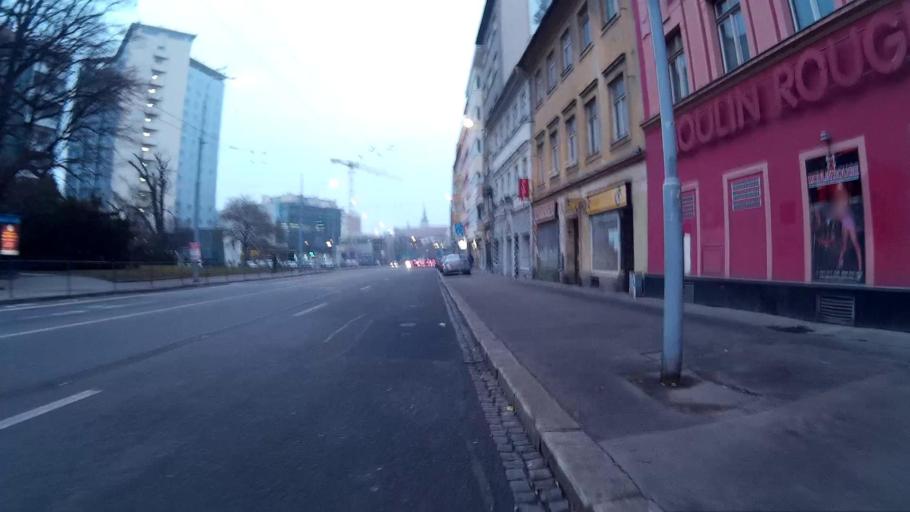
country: CZ
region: South Moravian
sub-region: Mesto Brno
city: Brno
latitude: 49.2007
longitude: 16.6029
